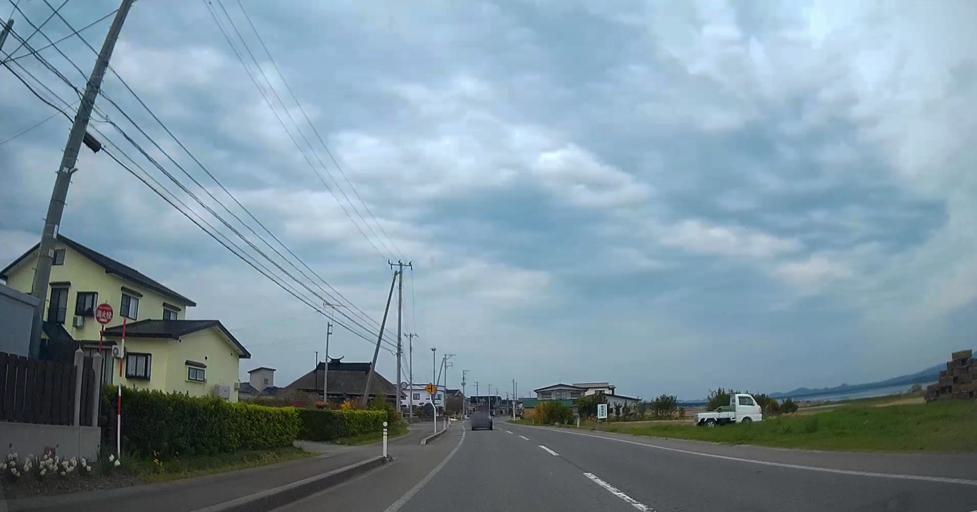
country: JP
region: Aomori
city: Shimokizukuri
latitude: 40.9989
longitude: 140.3452
